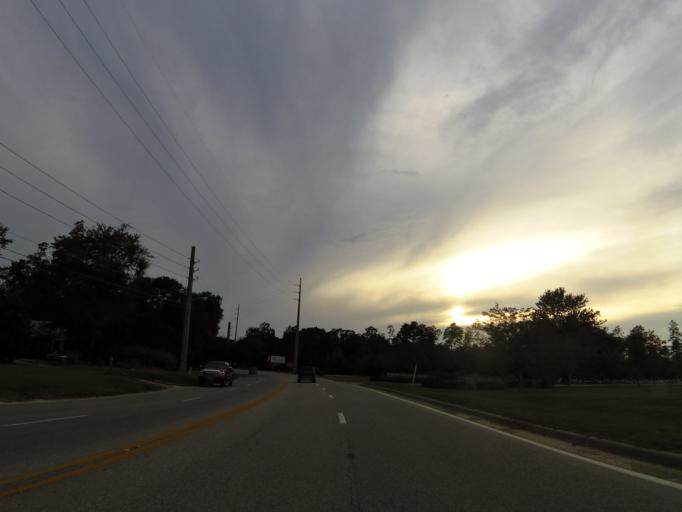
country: US
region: Alabama
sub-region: Baldwin County
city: Bay Minette
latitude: 30.8902
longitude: -87.7606
